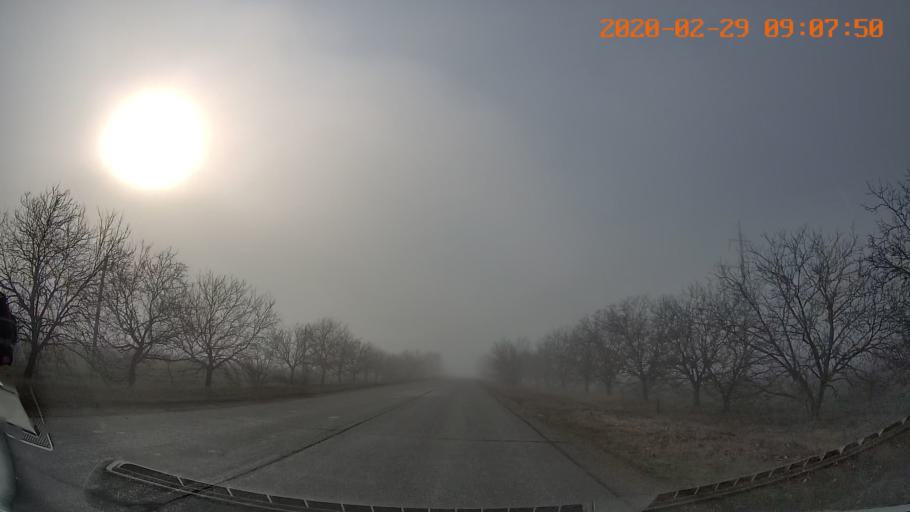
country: MD
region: Telenesti
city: Tiraspolul Nou
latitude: 46.8577
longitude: 29.7503
